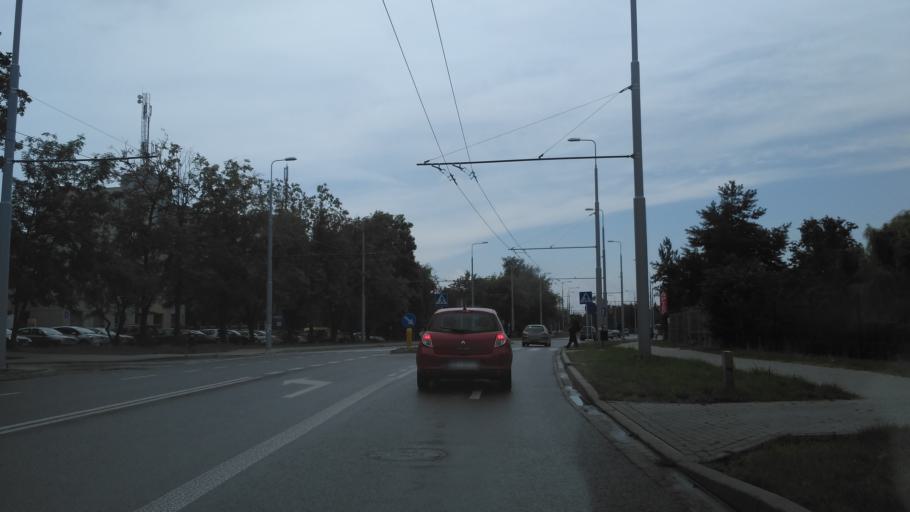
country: PL
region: Lublin Voivodeship
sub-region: Powiat lubelski
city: Lublin
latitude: 51.2057
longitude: 22.5868
